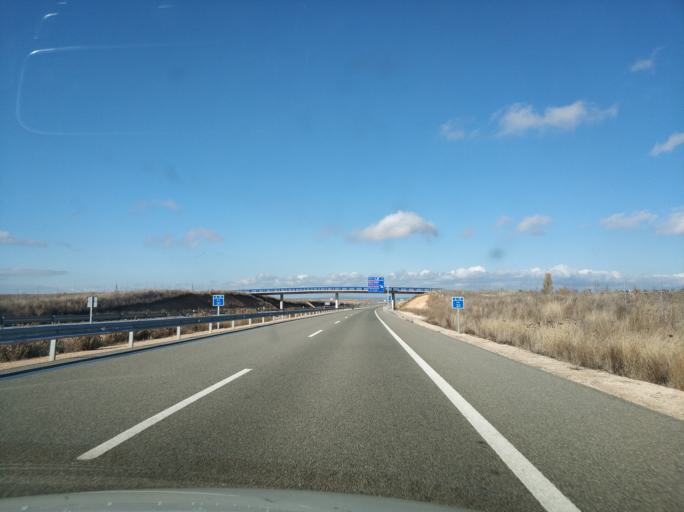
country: ES
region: Castille and Leon
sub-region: Provincia de Soria
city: Coscurita
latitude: 41.4097
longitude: -2.4834
